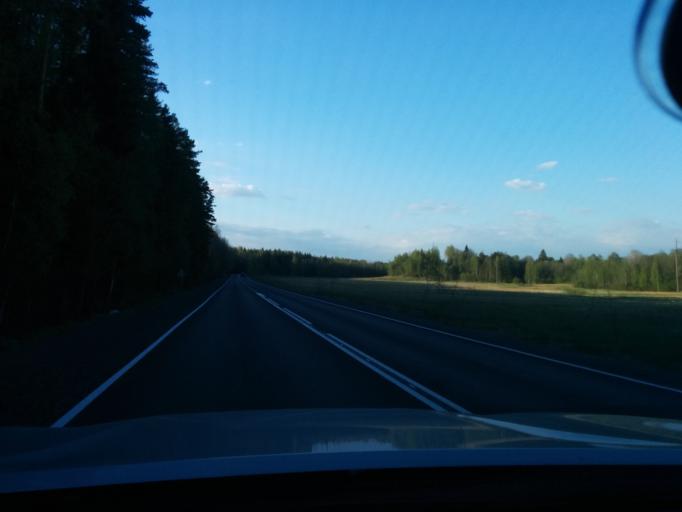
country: RU
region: Leningrad
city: Verkhniye Osel'ki
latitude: 60.1904
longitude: 30.4127
